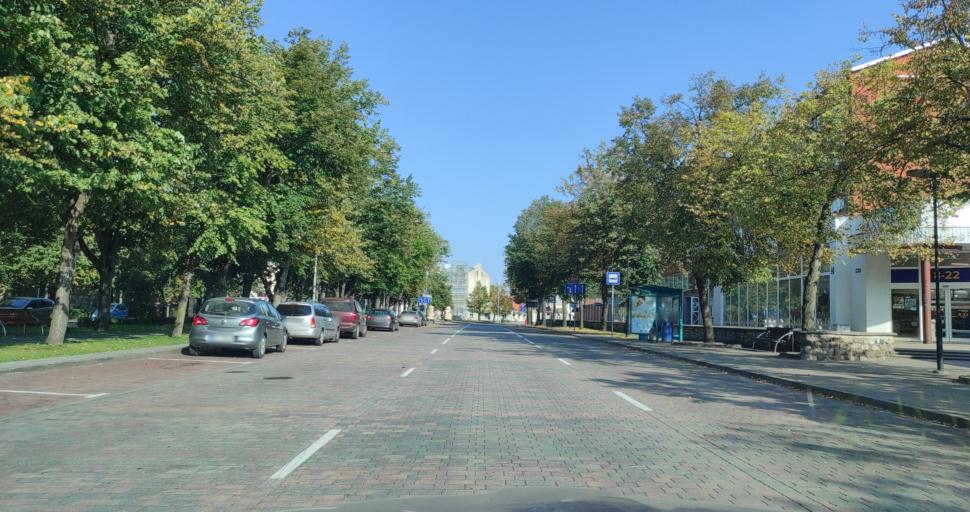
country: LV
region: Ventspils
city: Ventspils
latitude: 57.3921
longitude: 21.5641
